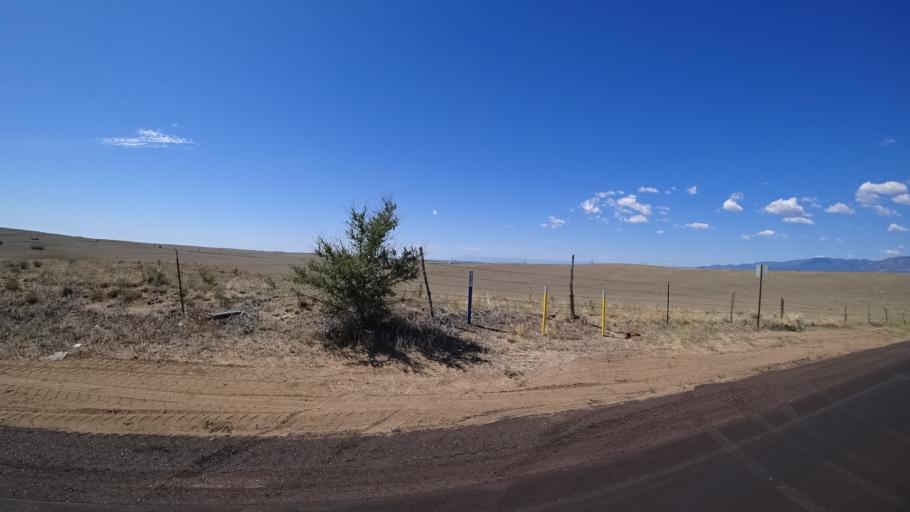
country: US
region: Colorado
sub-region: El Paso County
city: Security-Widefield
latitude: 38.7810
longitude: -104.6177
